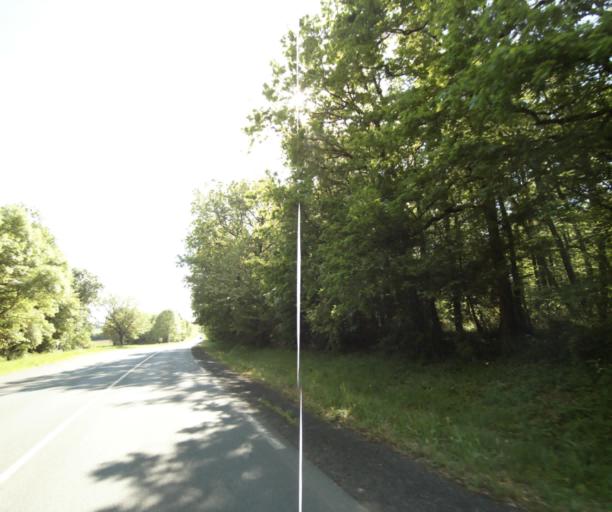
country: FR
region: Poitou-Charentes
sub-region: Departement de la Charente-Maritime
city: Nieul-les-Saintes
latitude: 45.7091
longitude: -0.7549
